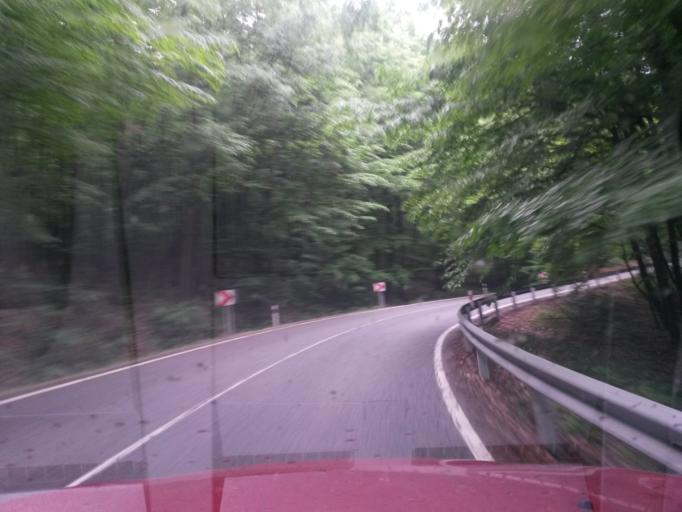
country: SK
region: Kosicky
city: Kosice
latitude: 48.7116
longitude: 21.1939
